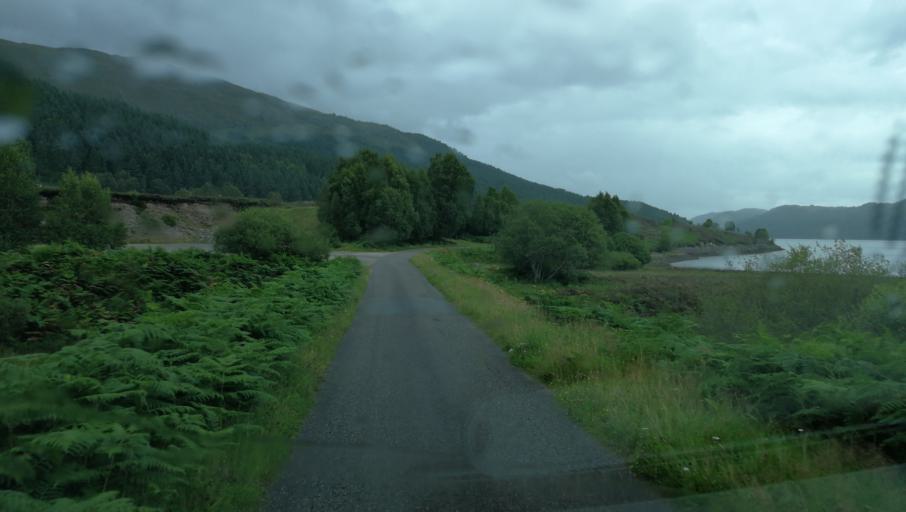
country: GB
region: Scotland
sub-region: Highland
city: Spean Bridge
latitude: 57.2701
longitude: -4.9669
